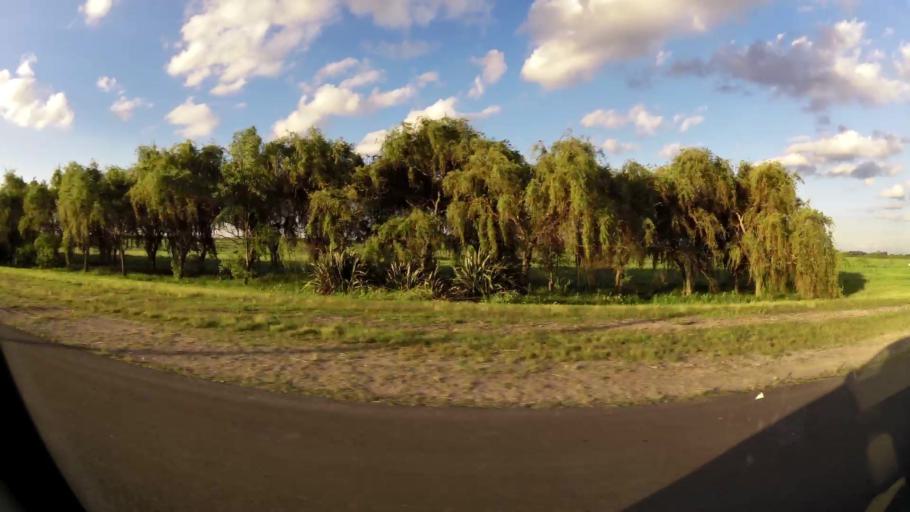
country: AR
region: Buenos Aires
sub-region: Partido de La Plata
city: La Plata
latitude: -34.8695
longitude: -57.9915
